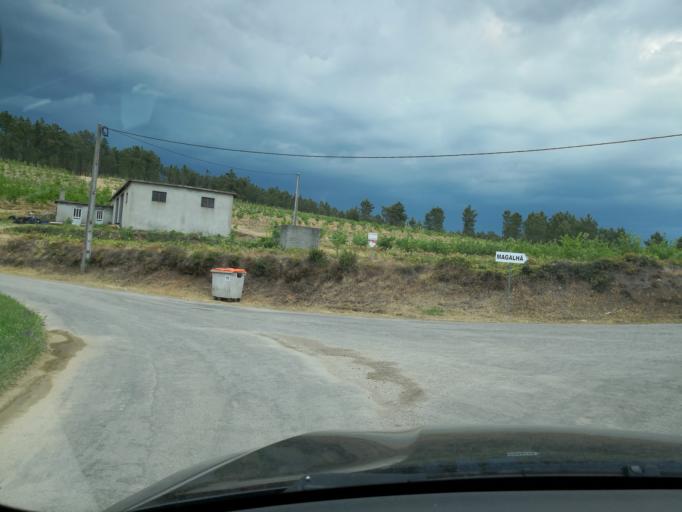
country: PT
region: Vila Real
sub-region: Sabrosa
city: Vilela
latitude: 41.2440
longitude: -7.6605
